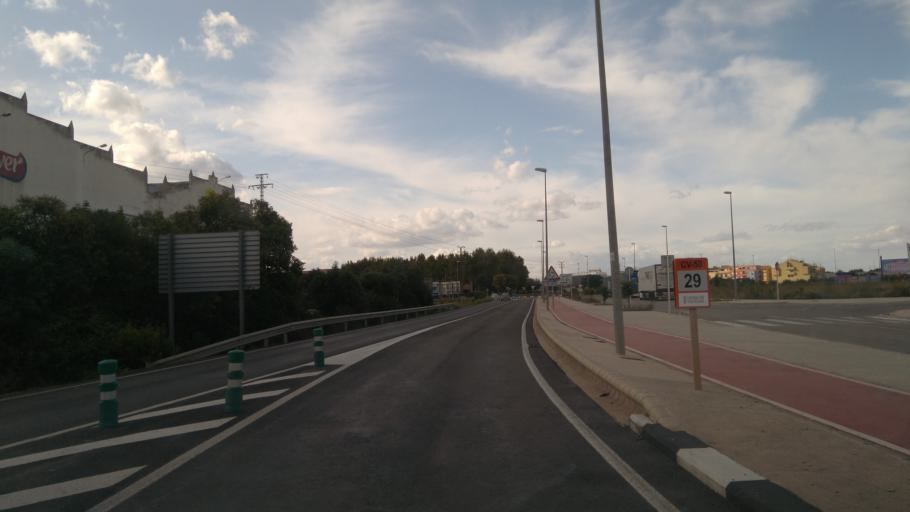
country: ES
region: Valencia
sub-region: Provincia de Valencia
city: L'Alcudia
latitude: 39.1947
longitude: -0.4971
